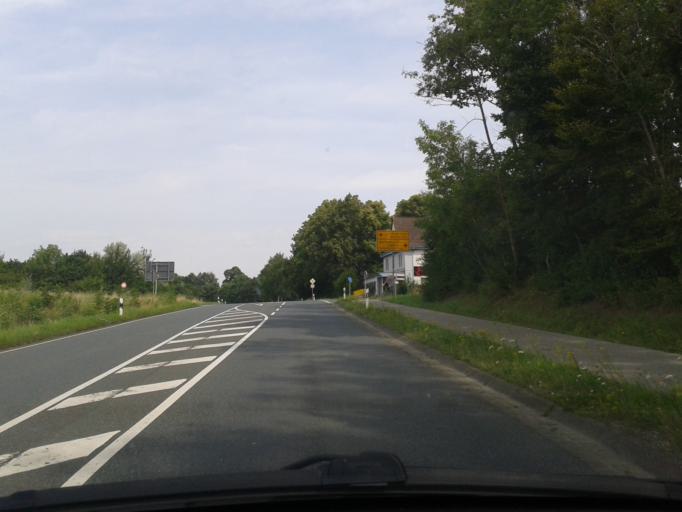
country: DE
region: North Rhine-Westphalia
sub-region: Regierungsbezirk Detmold
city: Barntrup
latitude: 51.9796
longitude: 9.1359
